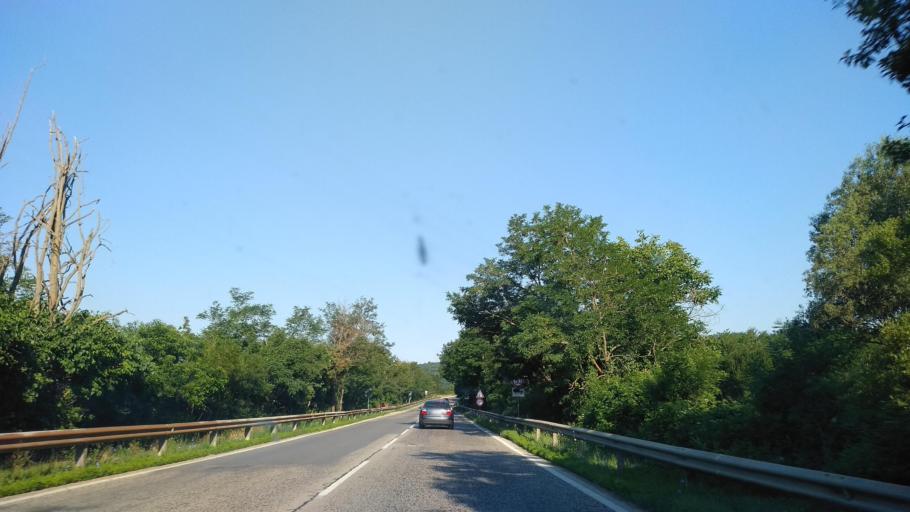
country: BG
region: Lovech
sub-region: Obshtina Lovech
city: Lovech
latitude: 43.0462
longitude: 24.8749
